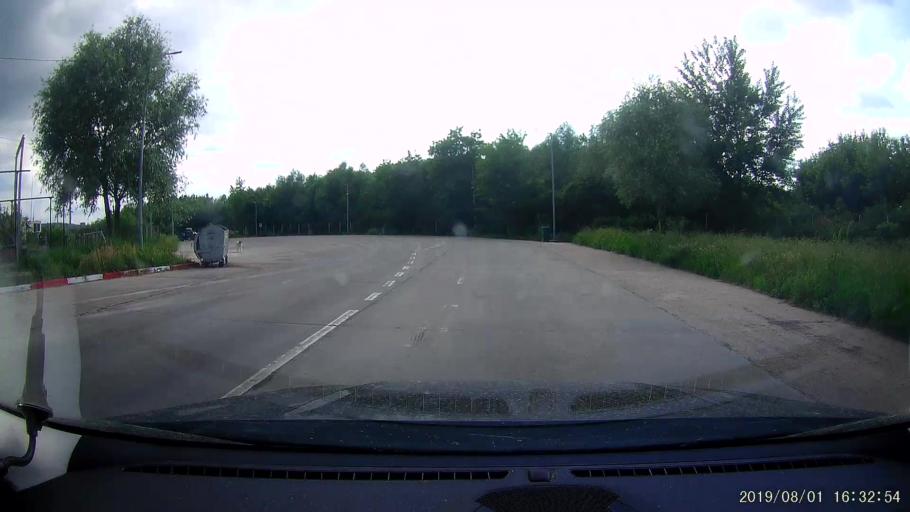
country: BG
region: Silistra
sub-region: Obshtina Silistra
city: Silistra
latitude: 44.1324
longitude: 27.2686
